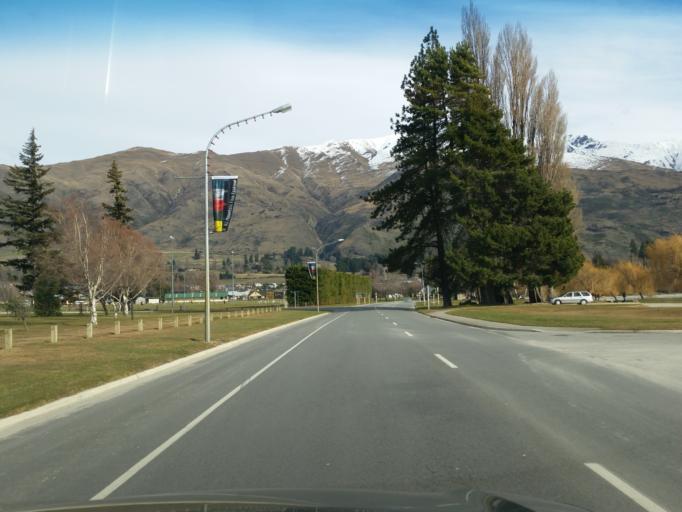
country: NZ
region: Otago
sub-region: Queenstown-Lakes District
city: Wanaka
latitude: -44.6983
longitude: 169.1287
